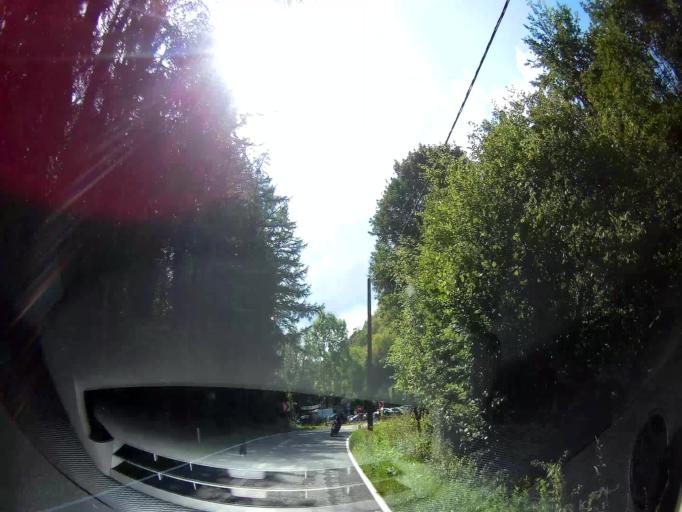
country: BE
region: Wallonia
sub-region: Province de Namur
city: Anhee
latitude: 50.3143
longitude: 4.8353
